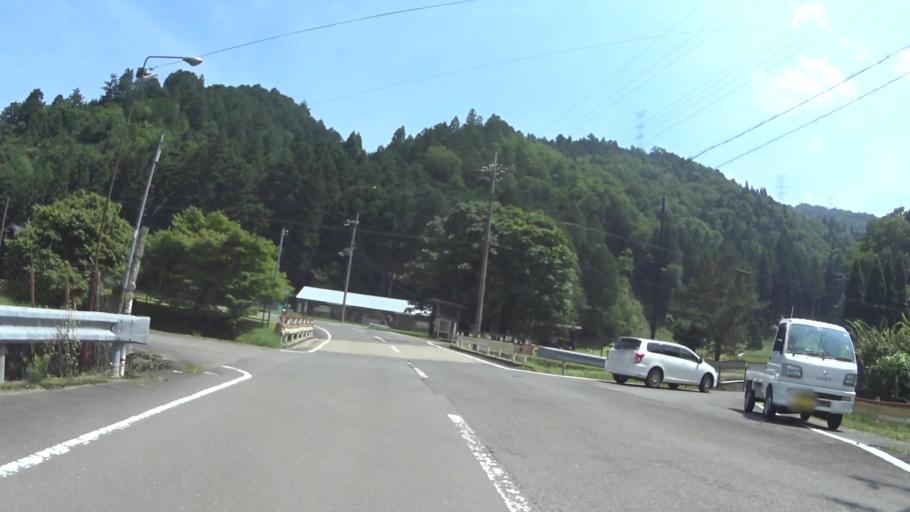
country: JP
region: Kyoto
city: Maizuru
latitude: 35.3312
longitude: 135.5404
